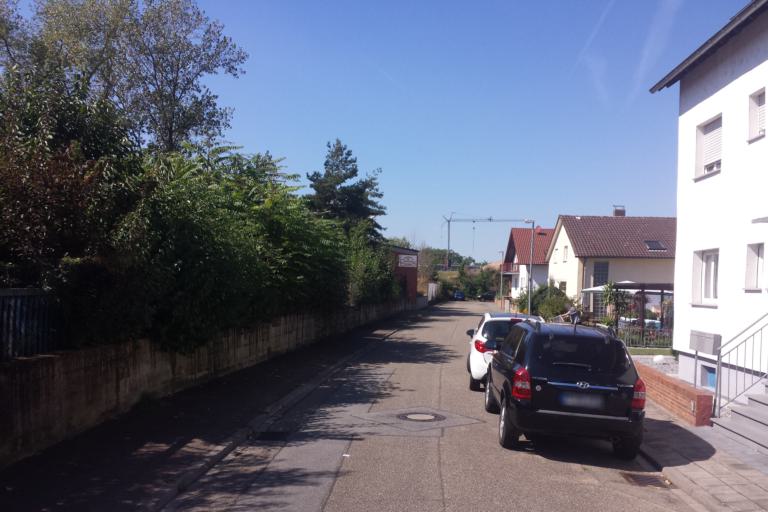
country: DE
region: Hesse
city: Viernheim
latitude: 49.5473
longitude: 8.5890
